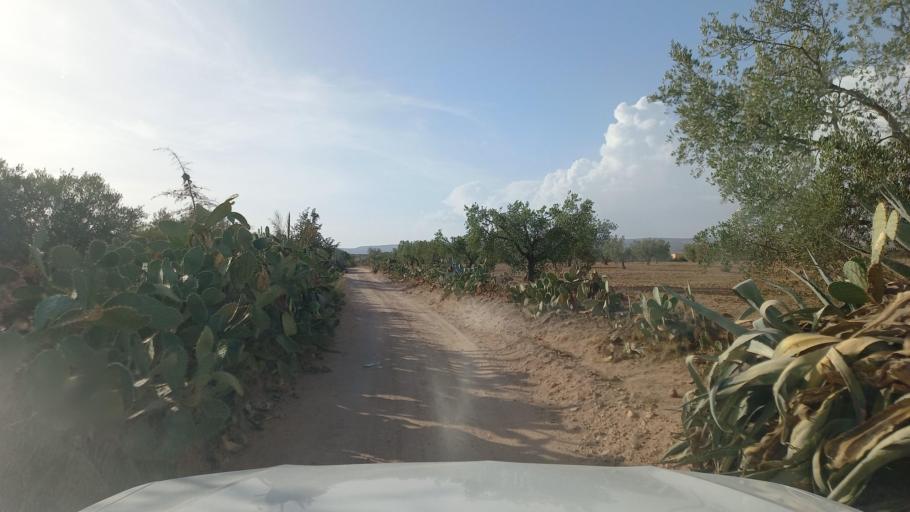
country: TN
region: Al Qasrayn
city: Kasserine
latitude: 35.2298
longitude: 8.9270
